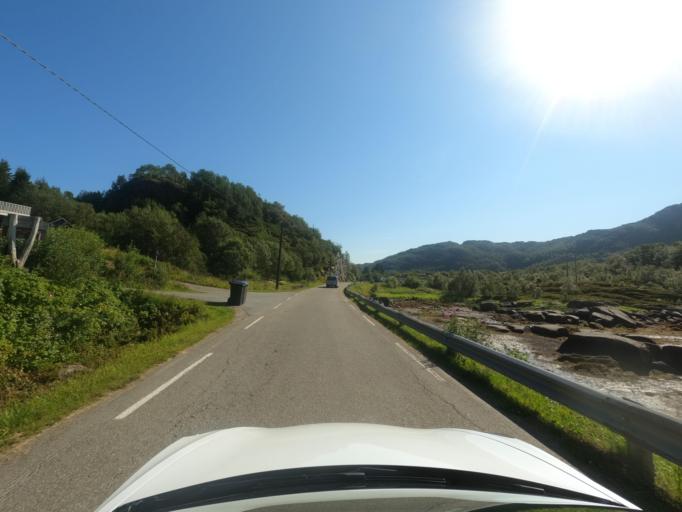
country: NO
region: Nordland
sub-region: Hadsel
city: Stokmarknes
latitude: 68.3044
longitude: 15.0091
